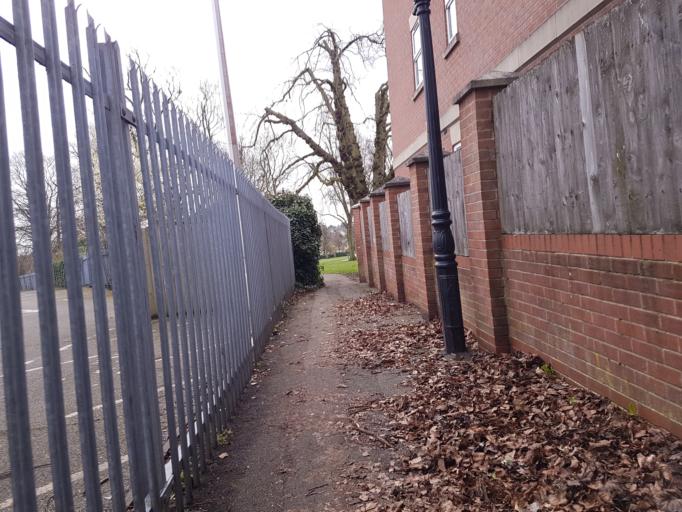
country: GB
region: England
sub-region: Leicestershire
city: Hinckley
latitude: 52.5420
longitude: -1.3639
